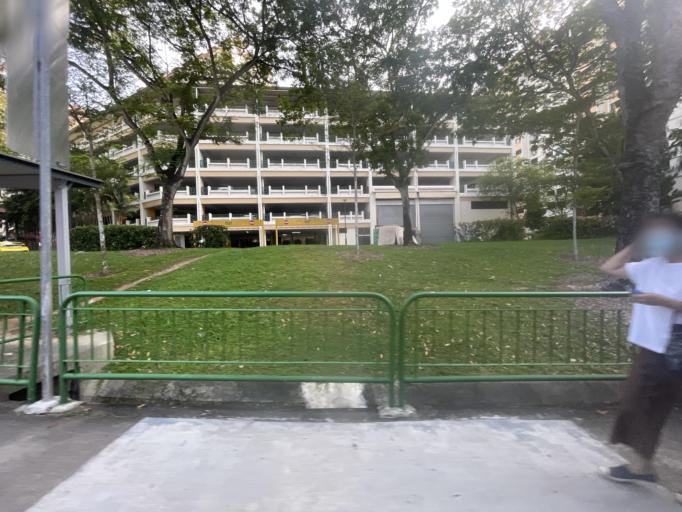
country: SG
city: Singapore
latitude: 1.3080
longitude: 103.7935
